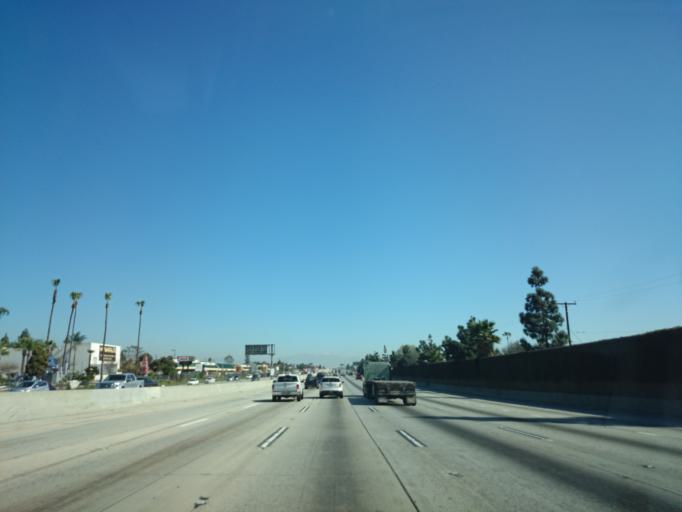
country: US
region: California
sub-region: San Bernardino County
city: Montclair
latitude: 34.0872
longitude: -117.6788
